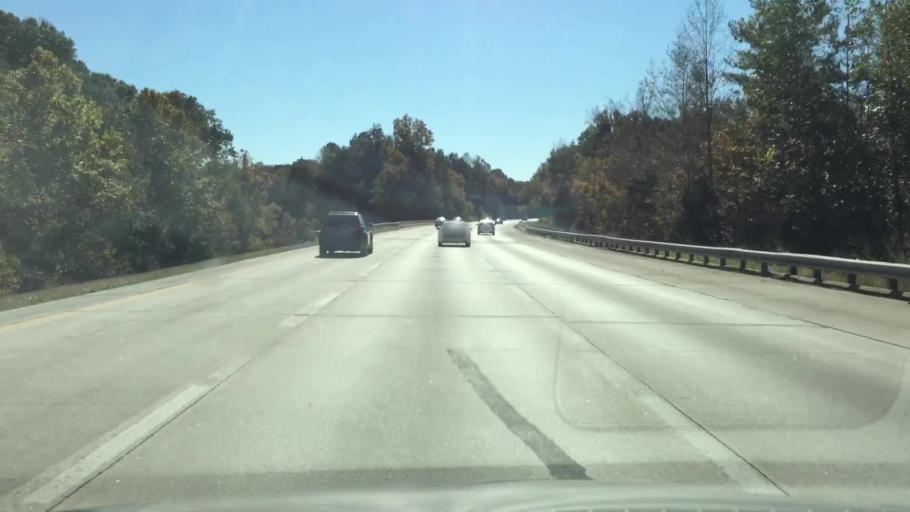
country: US
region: North Carolina
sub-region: Guilford County
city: Jamestown
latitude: 35.9453
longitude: -79.9024
